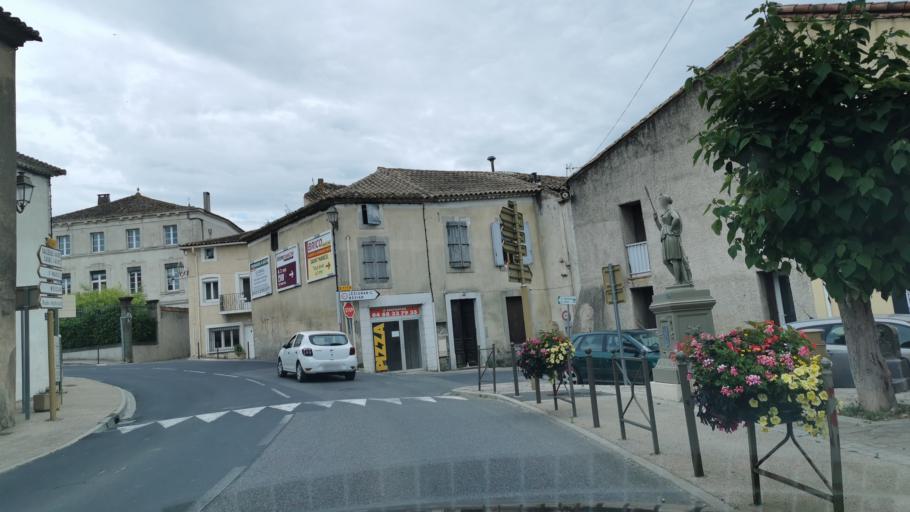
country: FR
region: Languedoc-Roussillon
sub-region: Departement de l'Aude
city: Marcorignan
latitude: 43.2261
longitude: 2.9221
